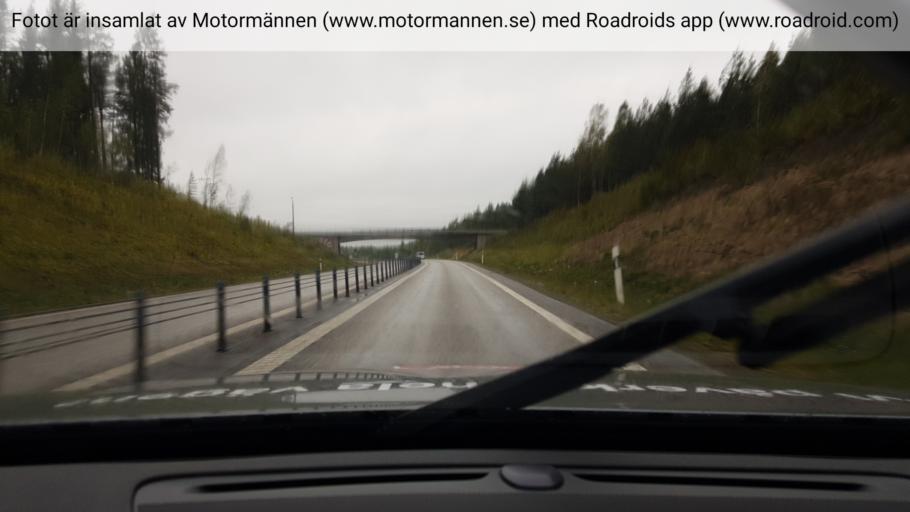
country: SE
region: OErebro
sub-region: Karlskoga Kommun
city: Karlskoga
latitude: 59.3252
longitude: 14.4455
